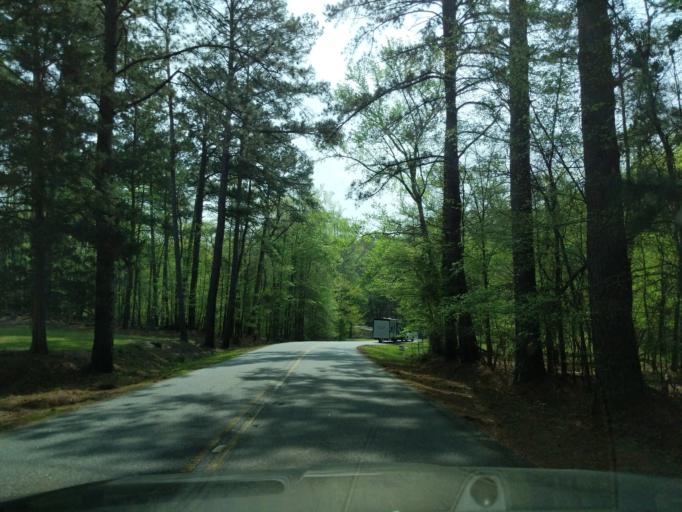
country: US
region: Georgia
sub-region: Lincoln County
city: Lincolnton
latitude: 33.8511
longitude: -82.4021
